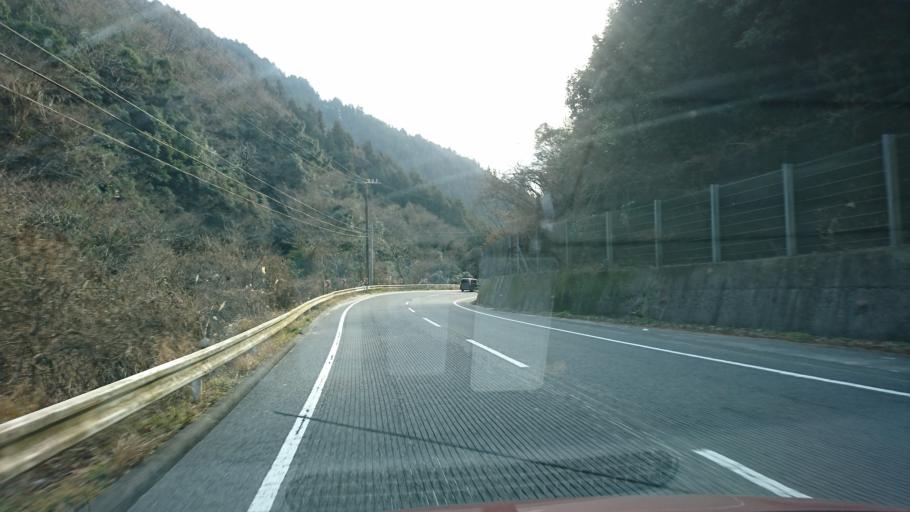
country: JP
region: Ehime
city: Hojo
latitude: 33.9137
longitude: 132.8799
